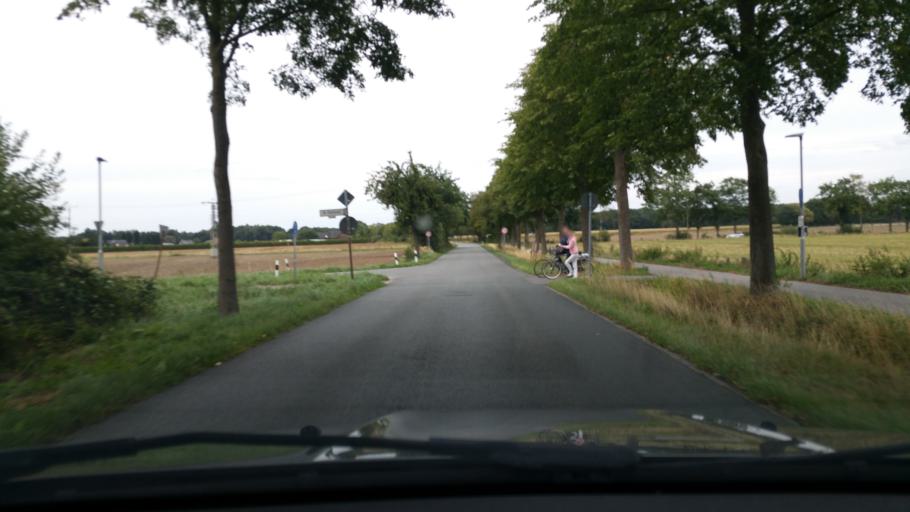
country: DE
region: North Rhine-Westphalia
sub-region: Regierungsbezirk Dusseldorf
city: Bocholt
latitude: 51.8591
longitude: 6.6340
